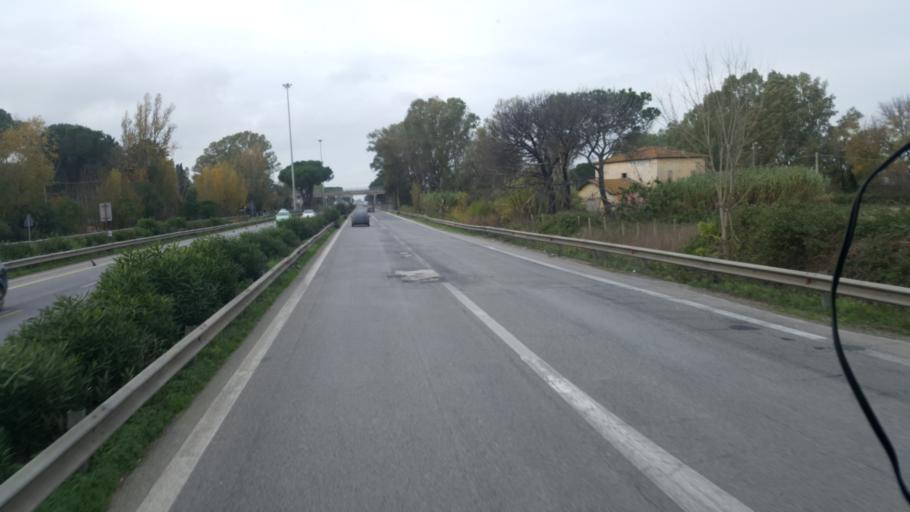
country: IT
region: Latium
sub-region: Provincia di Latina
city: Borgo Podgora
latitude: 41.4873
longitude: 12.8492
